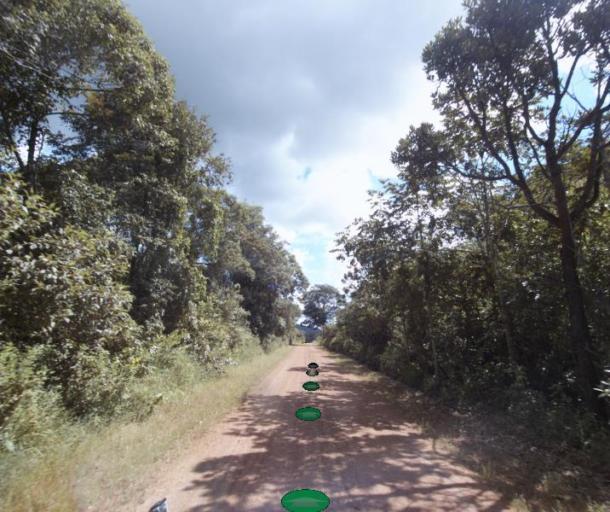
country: BR
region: Goias
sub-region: Pirenopolis
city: Pirenopolis
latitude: -15.7887
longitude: -48.8751
